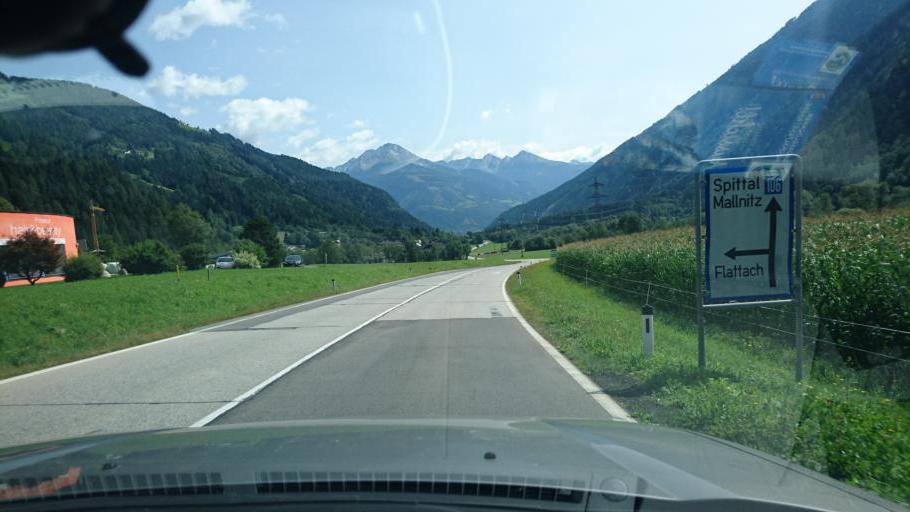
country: AT
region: Carinthia
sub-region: Politischer Bezirk Spittal an der Drau
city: Flattach
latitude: 46.9335
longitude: 13.1207
